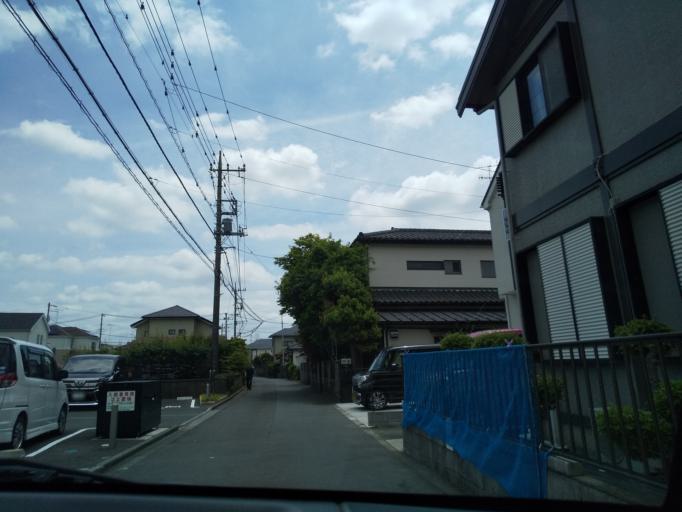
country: JP
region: Kanagawa
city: Zama
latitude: 35.5629
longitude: 139.3520
